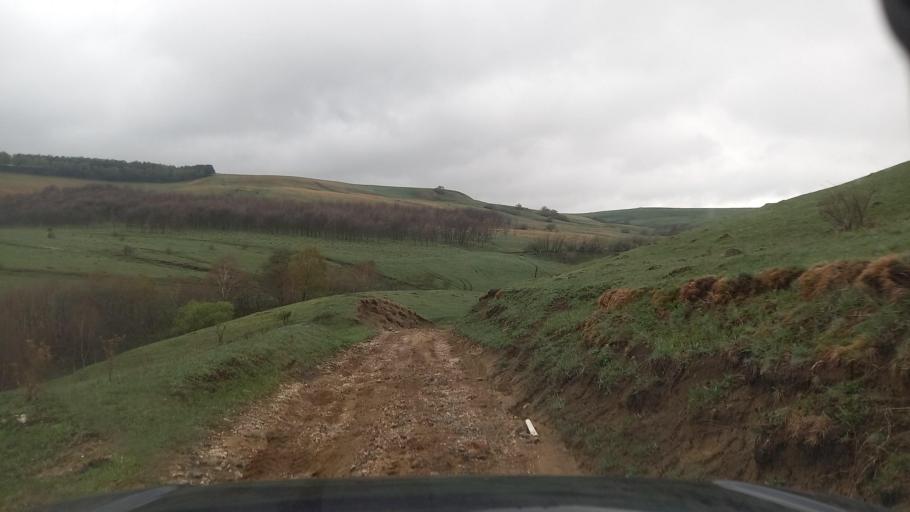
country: RU
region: Stavropol'skiy
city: Nezhinskiy
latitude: 43.8572
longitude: 42.6370
